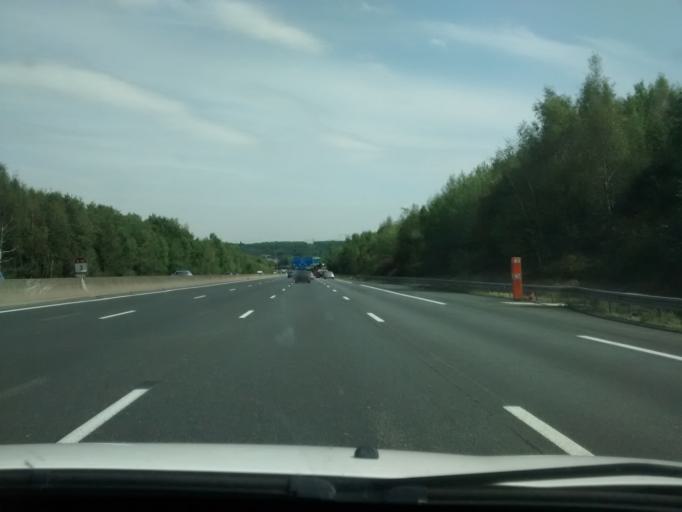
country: FR
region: Ile-de-France
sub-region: Departement de l'Essonne
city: Les Ulis
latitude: 48.6498
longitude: 2.1699
